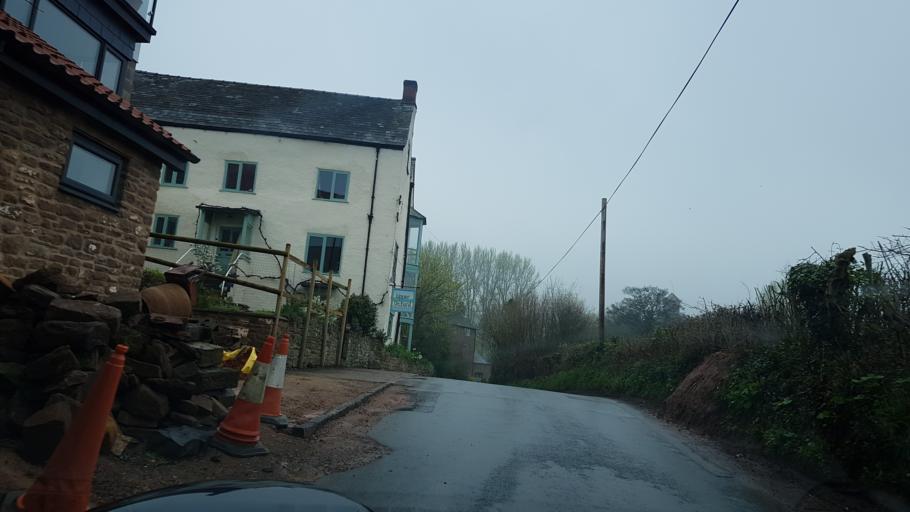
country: GB
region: England
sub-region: Herefordshire
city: Sellack
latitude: 51.9590
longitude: -2.6634
